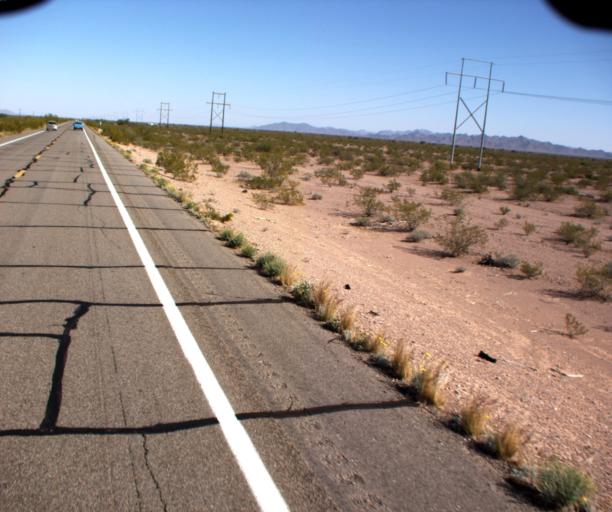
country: US
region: Arizona
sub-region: La Paz County
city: Quartzsite
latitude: 33.3821
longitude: -114.2171
